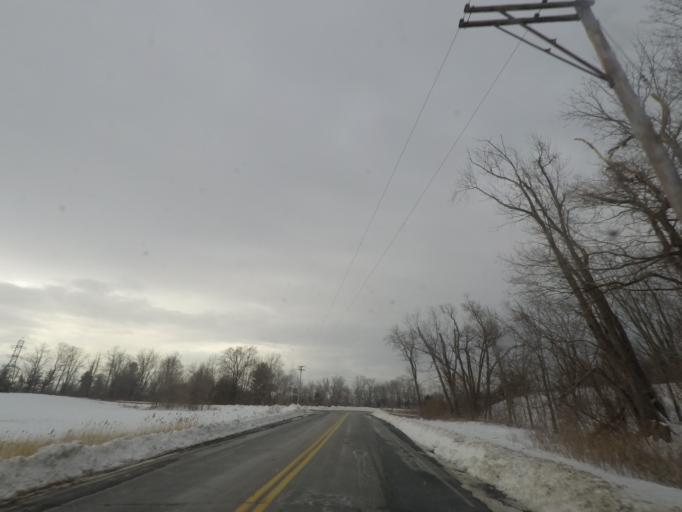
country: US
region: New York
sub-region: Rensselaer County
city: Castleton-on-Hudson
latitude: 42.4971
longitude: -73.7411
